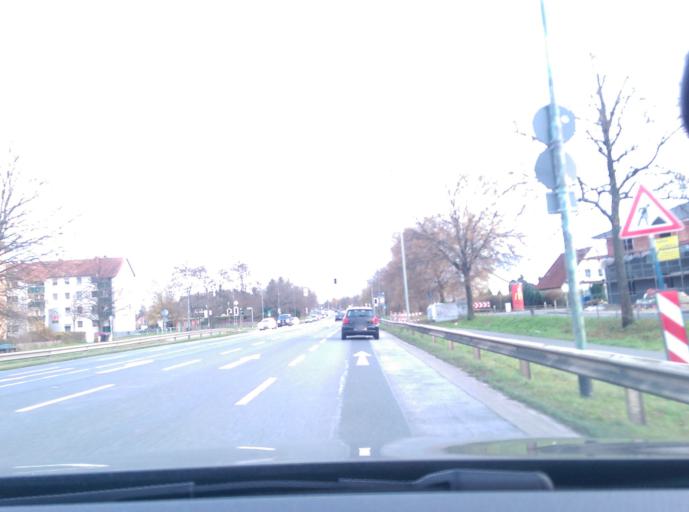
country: DE
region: Lower Saxony
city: Celle
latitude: 52.6084
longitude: 10.0484
